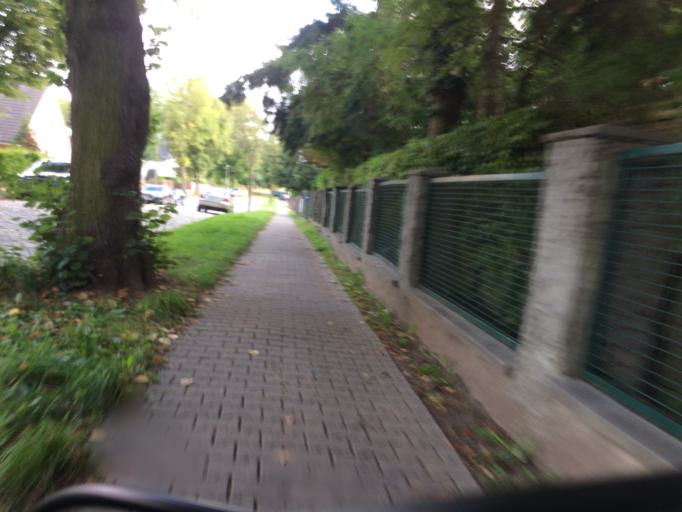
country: DE
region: Berlin
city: Blankenburg
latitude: 52.5930
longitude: 13.4582
